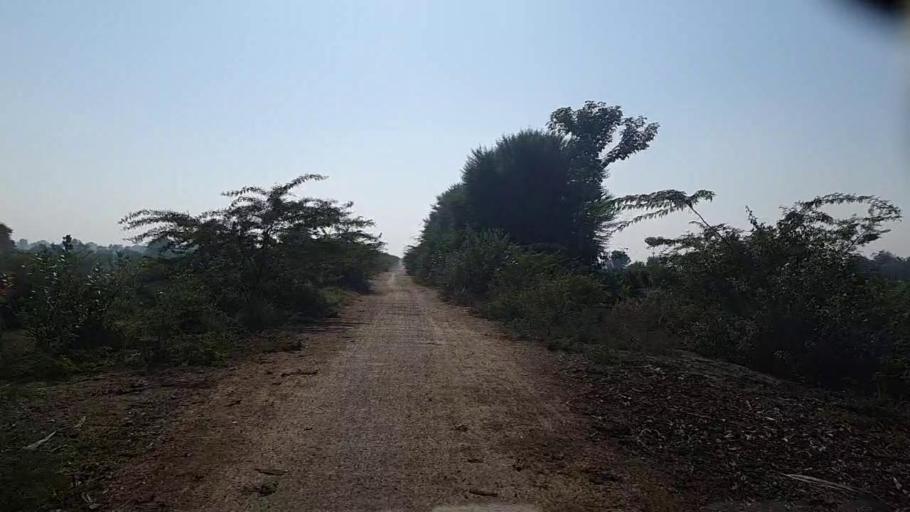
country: PK
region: Sindh
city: Pad Idan
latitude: 26.7832
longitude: 68.3358
